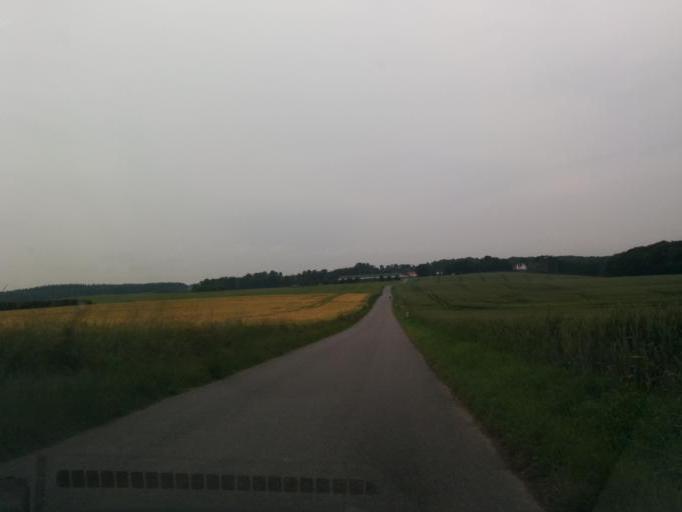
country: DK
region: Central Jutland
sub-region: Arhus Kommune
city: Logten
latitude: 56.2822
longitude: 10.3708
